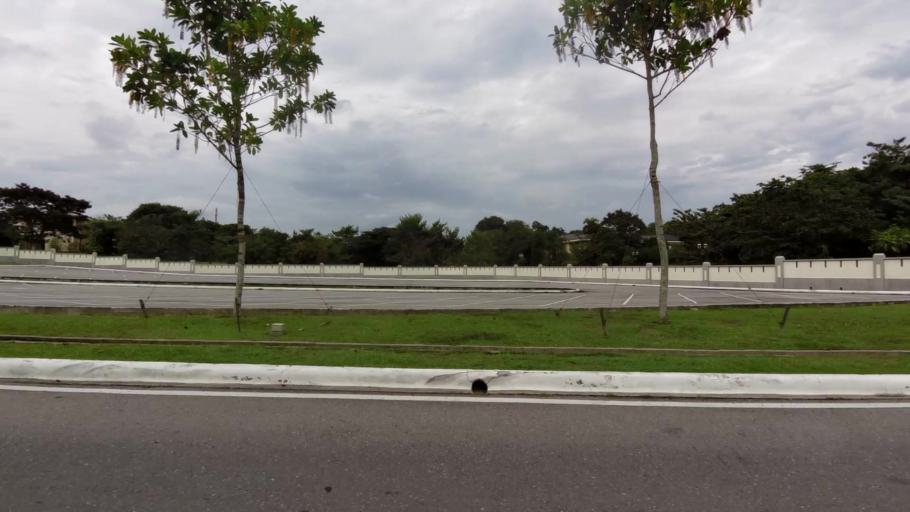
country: BN
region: Brunei and Muara
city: Bandar Seri Begawan
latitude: 4.9182
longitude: 114.9350
